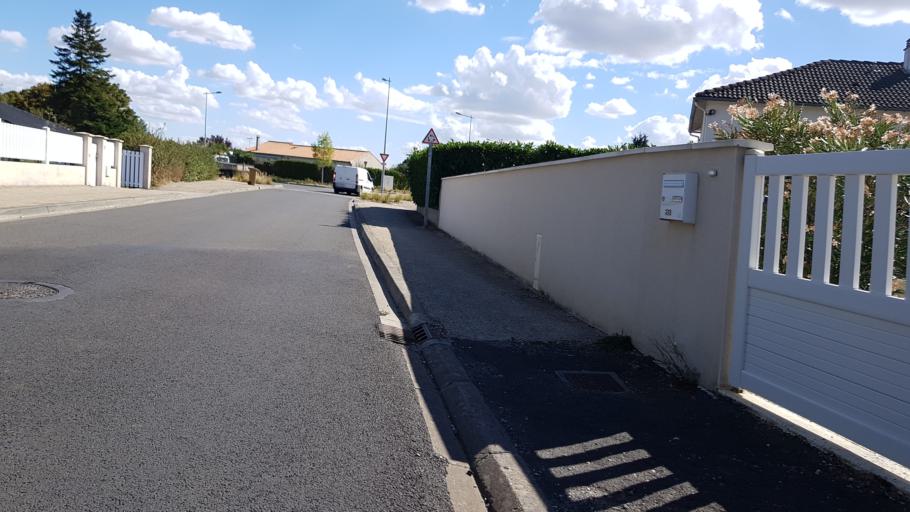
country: FR
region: Poitou-Charentes
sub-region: Departement des Deux-Sevres
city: Vouille
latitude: 46.3154
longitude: -0.3606
